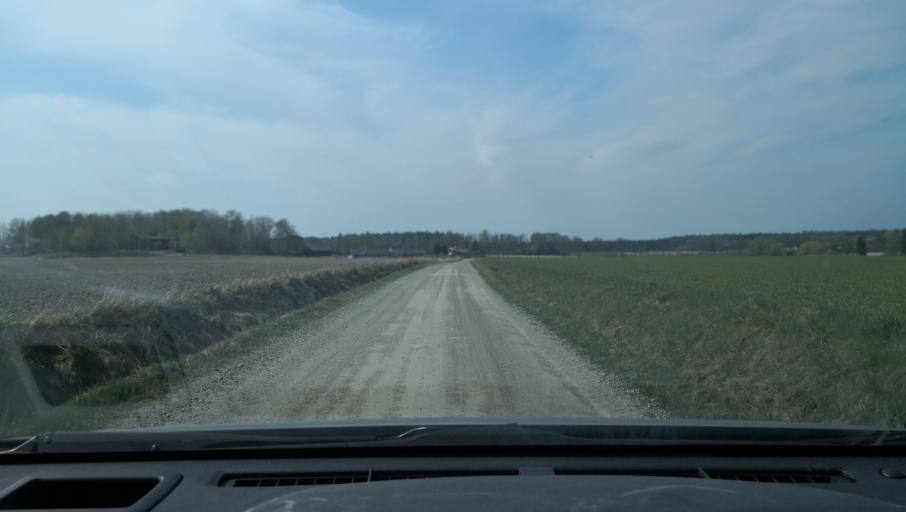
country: SE
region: Vaestmanland
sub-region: Vasteras
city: Skultuna
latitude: 59.7758
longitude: 16.3976
